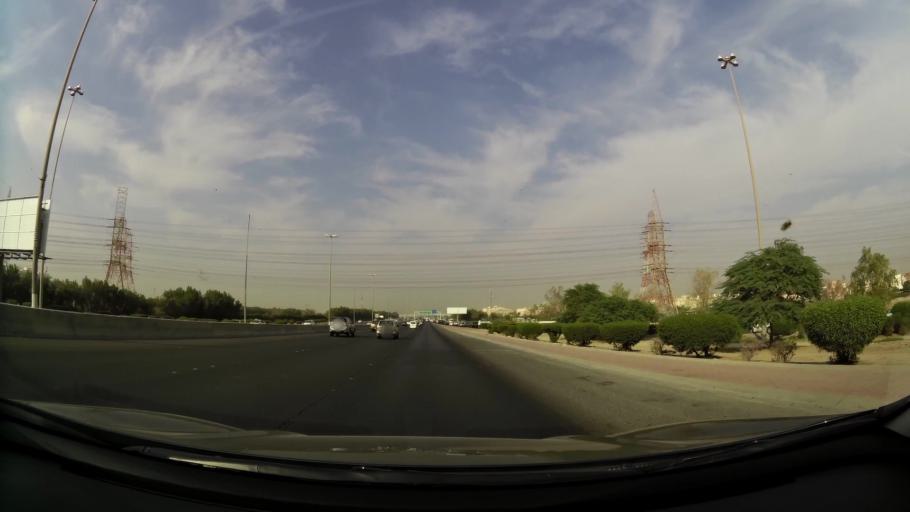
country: KW
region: Mubarak al Kabir
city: Sabah as Salim
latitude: 29.2650
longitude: 48.0381
